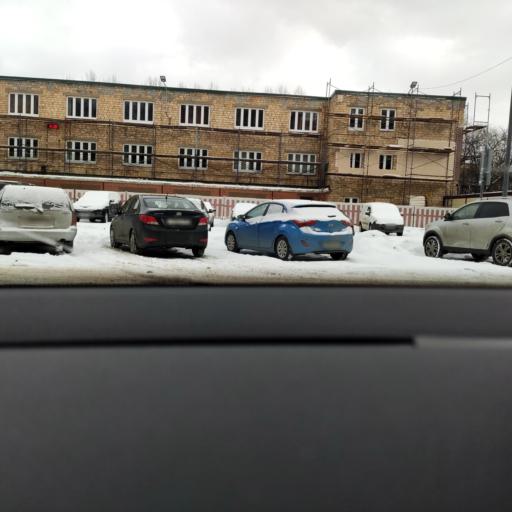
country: RU
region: Moskovskaya
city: Reutov
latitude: 55.7623
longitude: 37.8675
